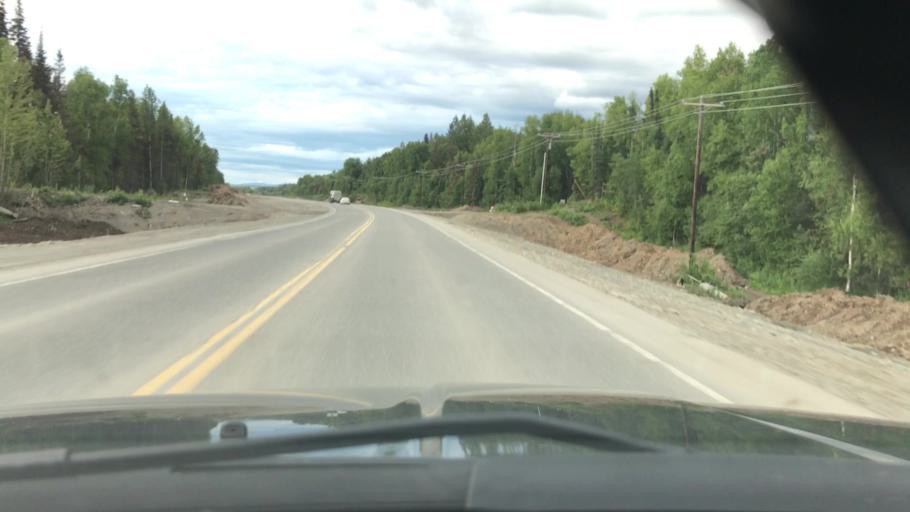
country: US
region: Alaska
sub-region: Matanuska-Susitna Borough
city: Y
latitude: 62.1126
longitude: -150.0534
